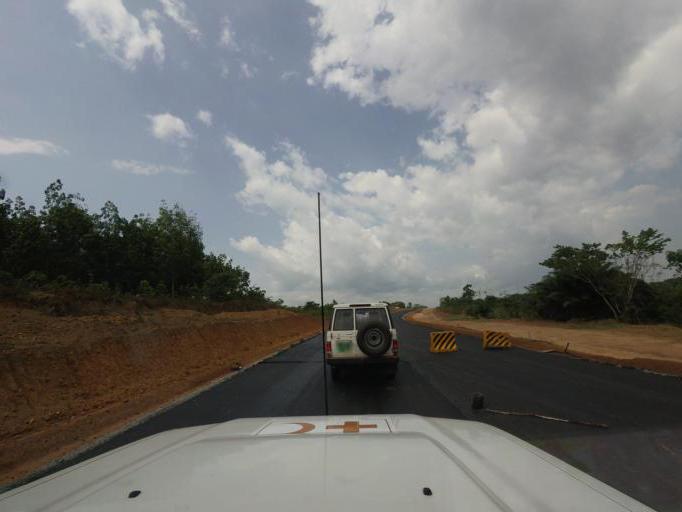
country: LR
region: Margibi
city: Kakata
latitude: 6.7371
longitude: -10.1234
